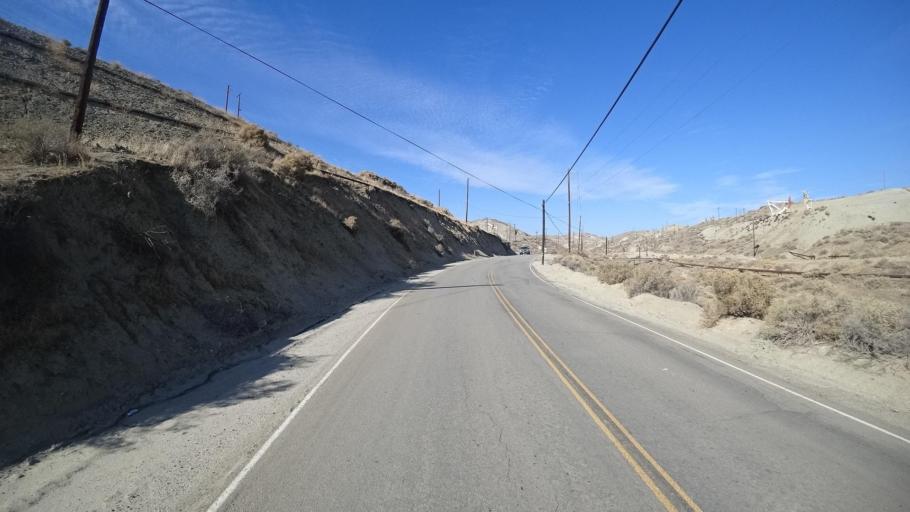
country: US
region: California
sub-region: Kern County
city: Oildale
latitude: 35.5688
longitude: -118.9579
